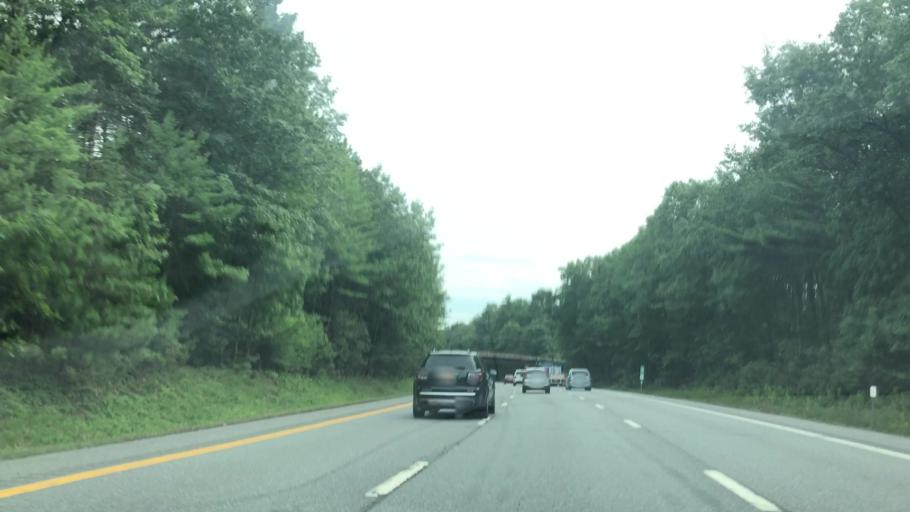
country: US
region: New York
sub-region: Warren County
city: West Glens Falls
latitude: 43.2437
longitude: -73.6913
